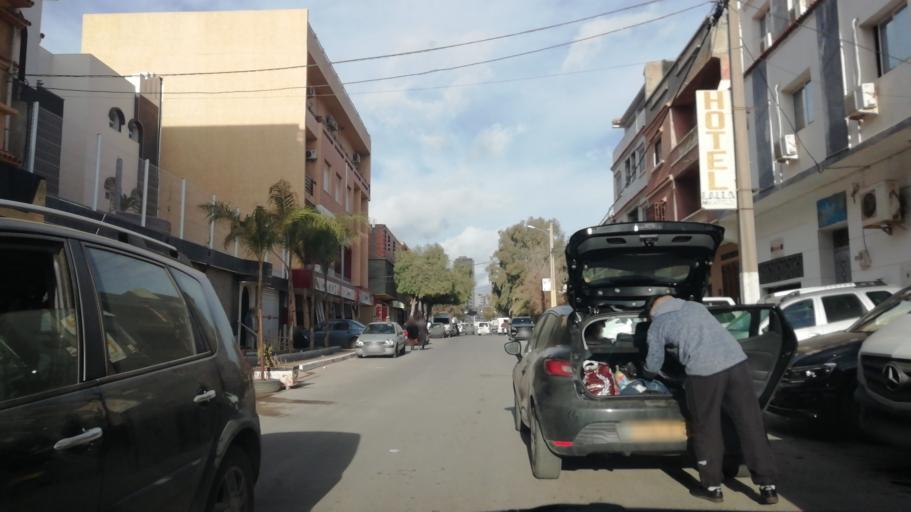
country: DZ
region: Oran
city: Bir el Djir
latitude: 35.7283
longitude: -0.5819
